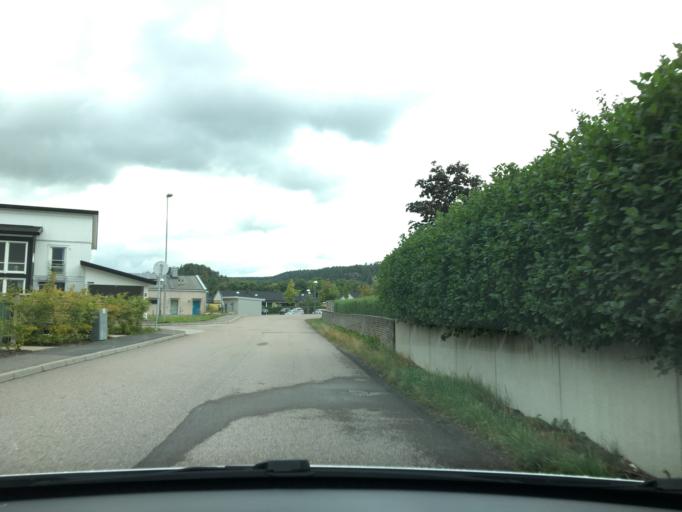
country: SE
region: Vaestra Goetaland
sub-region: Ale Kommun
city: Nodinge-Nol
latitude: 57.8880
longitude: 12.0592
